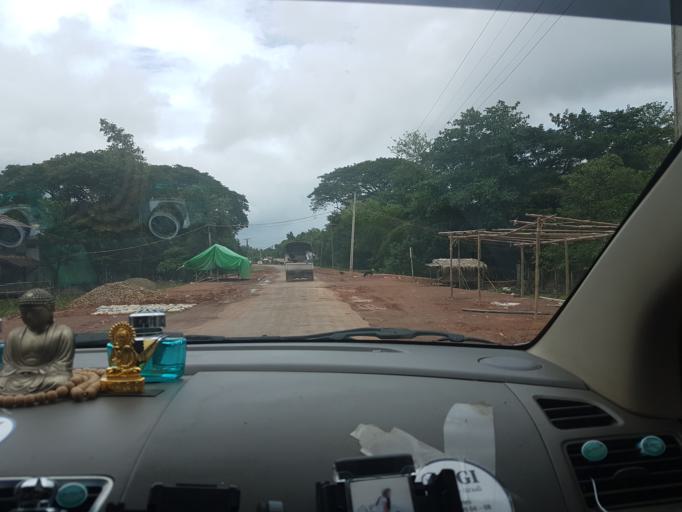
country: MM
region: Bago
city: Nyaunglebin
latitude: 17.9147
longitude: 96.8343
